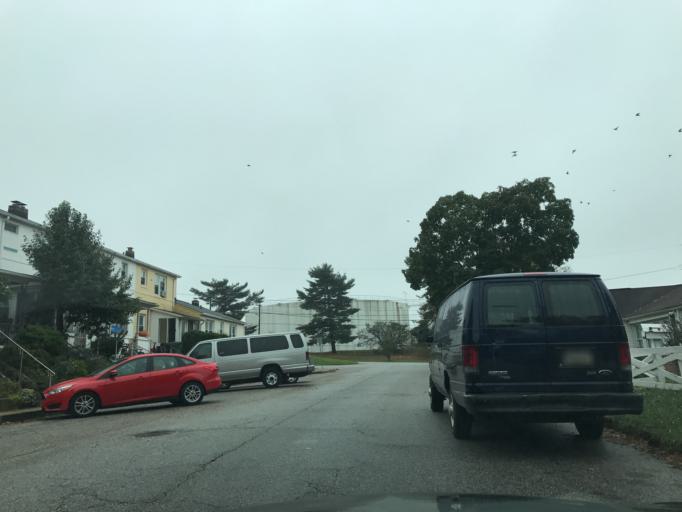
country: US
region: Maryland
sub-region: Baltimore County
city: Rosedale
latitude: 39.3049
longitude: -76.5547
